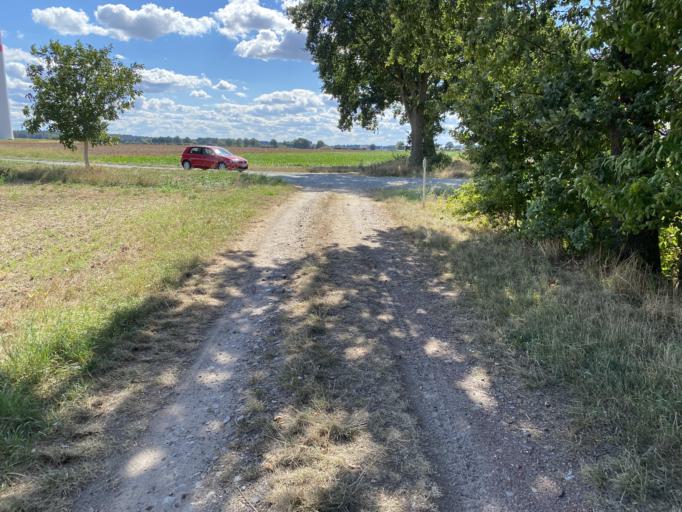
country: DE
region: Lower Saxony
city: Altenmedingen
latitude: 53.1562
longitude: 10.6451
